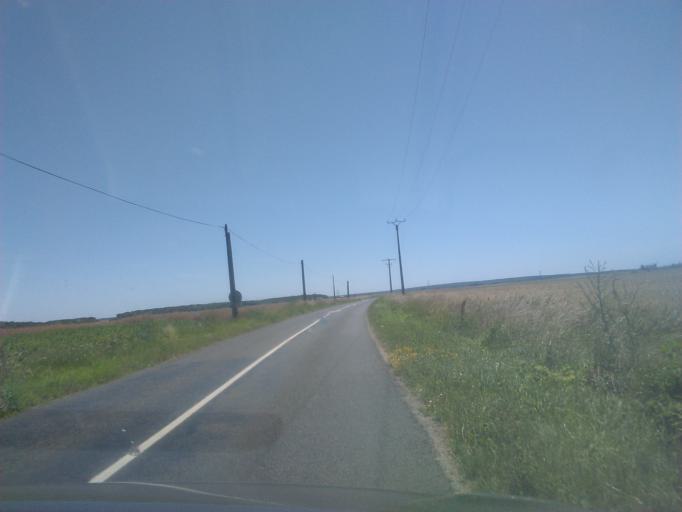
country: FR
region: Centre
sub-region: Departement du Loir-et-Cher
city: Herbault
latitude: 47.6478
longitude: 1.1881
